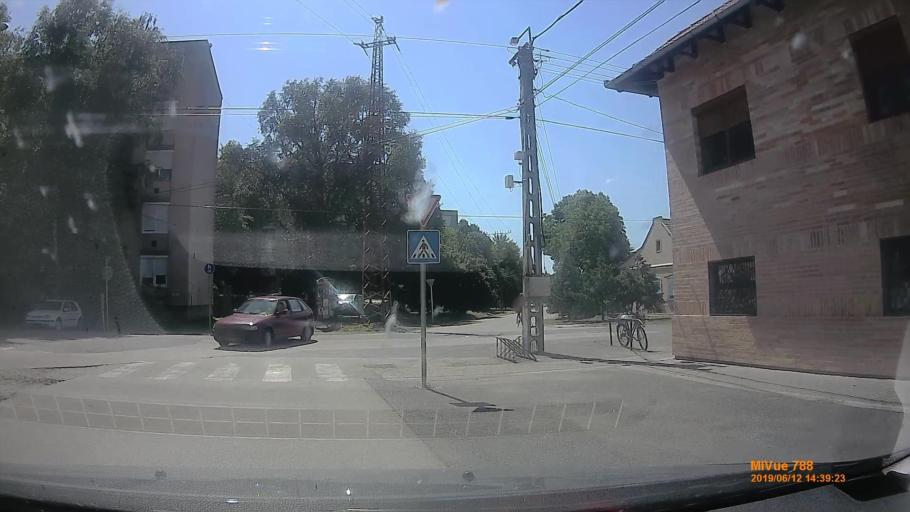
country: HU
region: Csongrad
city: Mako
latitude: 46.2096
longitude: 20.4704
